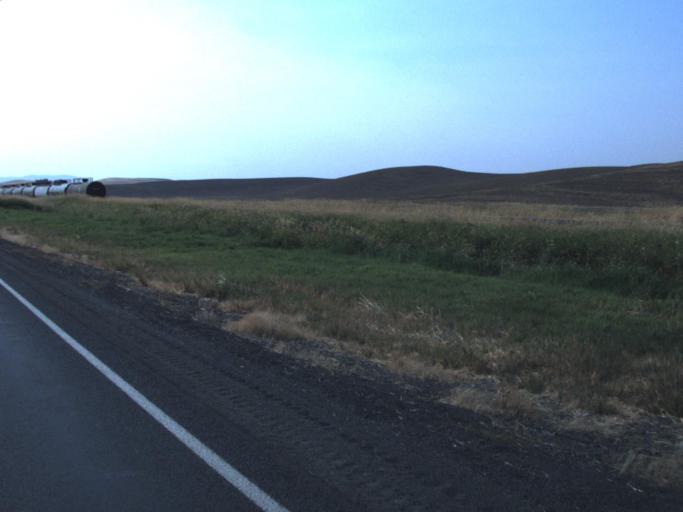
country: US
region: Washington
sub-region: Whitman County
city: Colfax
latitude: 47.0372
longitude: -117.1543
